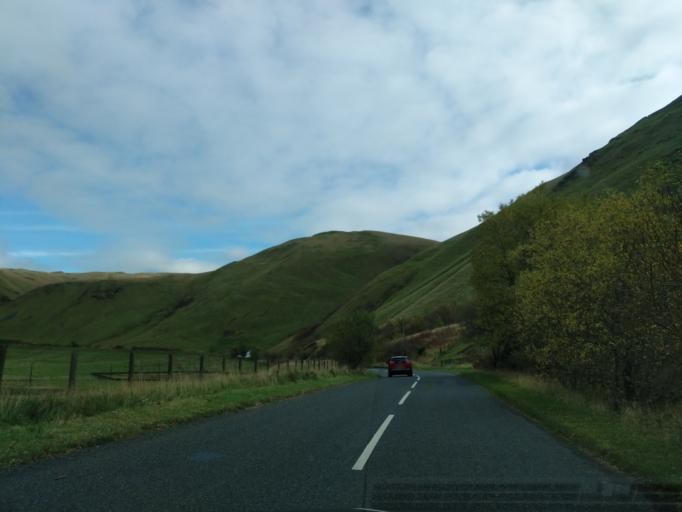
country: GB
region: Scotland
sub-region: Dumfries and Galloway
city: Thornhill
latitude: 55.3426
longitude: -3.7474
